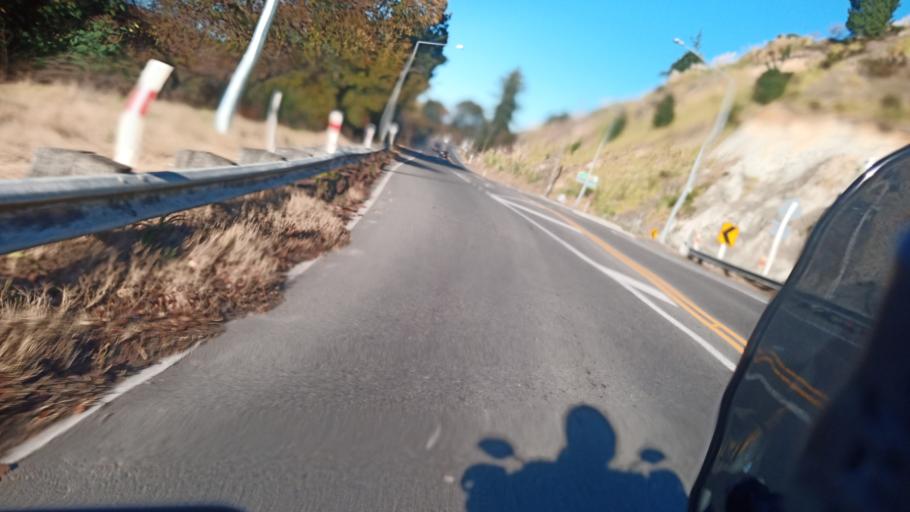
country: NZ
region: Hawke's Bay
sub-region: Napier City
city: Napier
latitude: -39.3950
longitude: 176.8759
